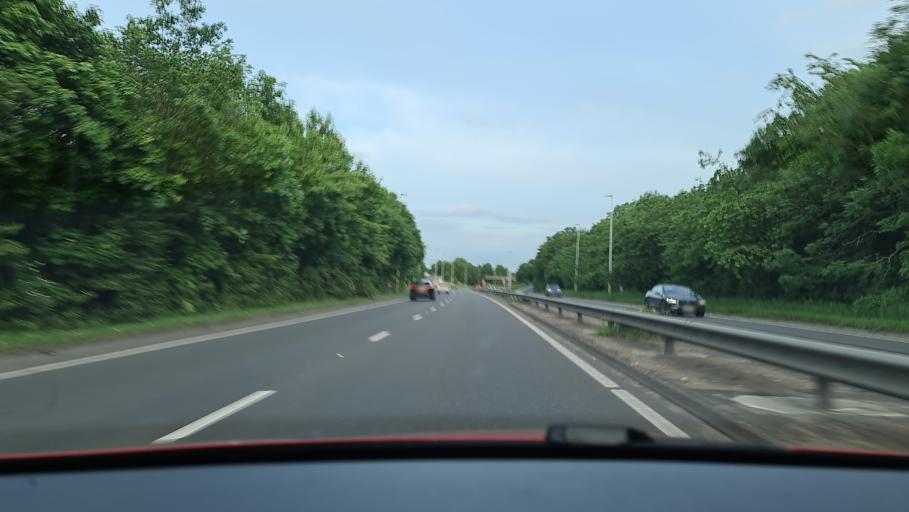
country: GB
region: England
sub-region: Peterborough
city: Peterborough
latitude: 52.5549
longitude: -0.2726
